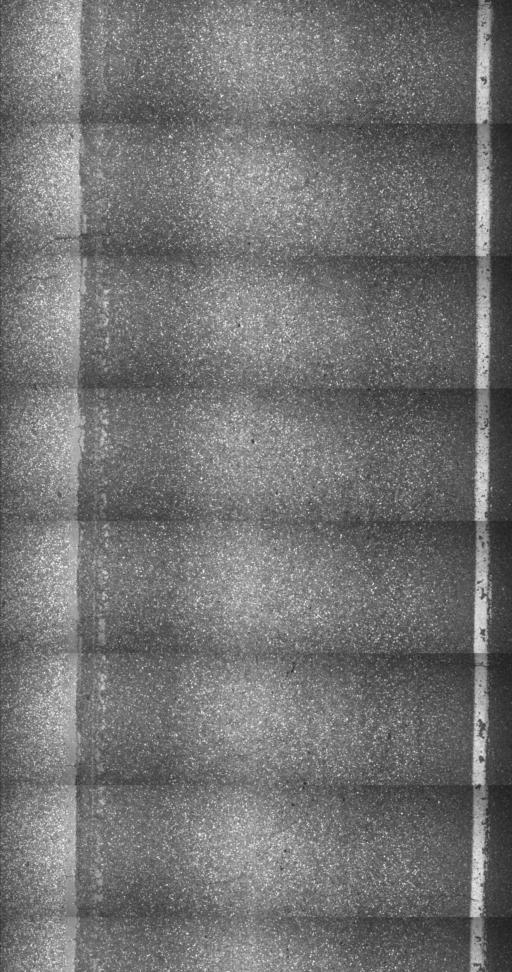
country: US
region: Vermont
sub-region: Franklin County
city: Enosburg Falls
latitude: 44.7948
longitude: -72.8802
